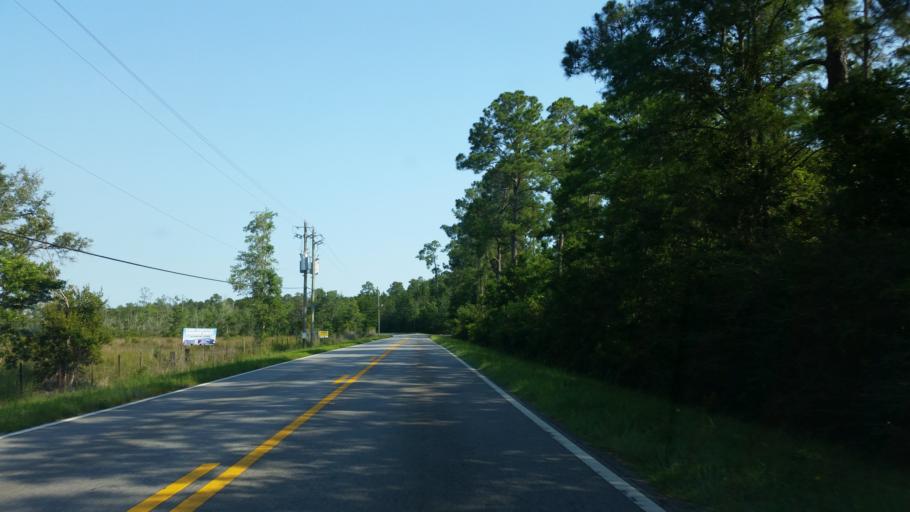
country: US
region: Florida
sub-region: Santa Rosa County
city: East Milton
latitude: 30.6009
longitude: -87.0073
